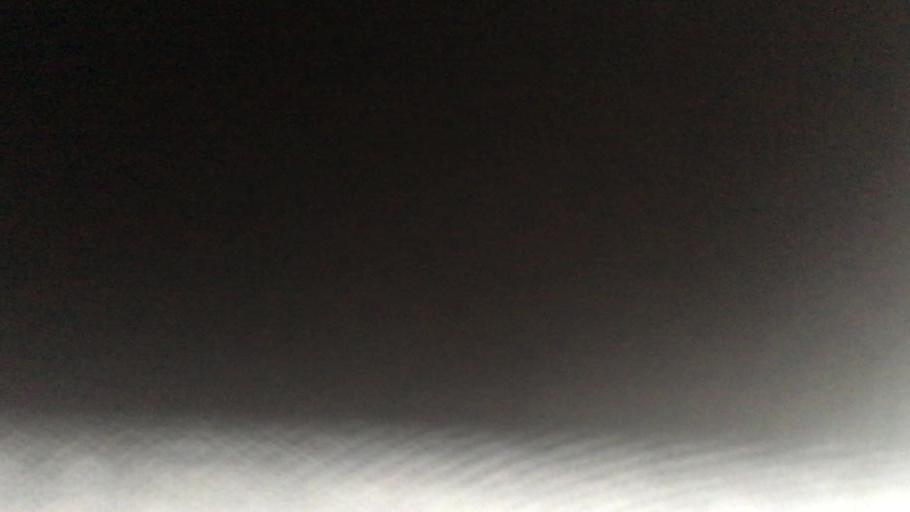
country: US
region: Maryland
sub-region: Montgomery County
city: Germantown
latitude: 39.1775
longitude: -77.2761
